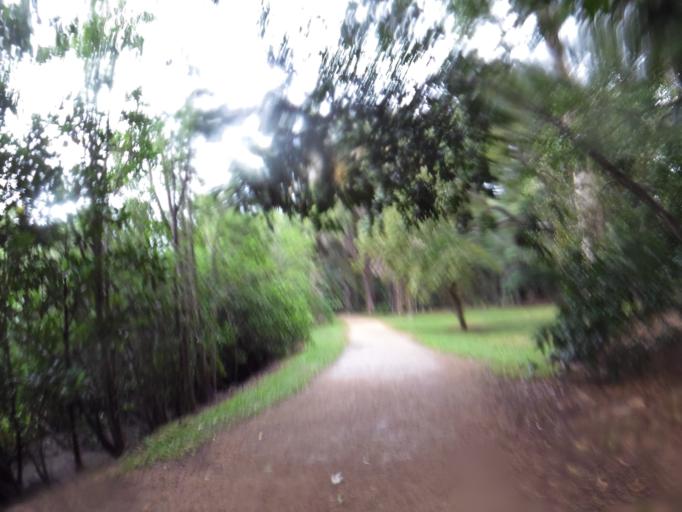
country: AU
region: Queensland
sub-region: Cairns
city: Cairns
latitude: -16.9016
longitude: 145.7510
